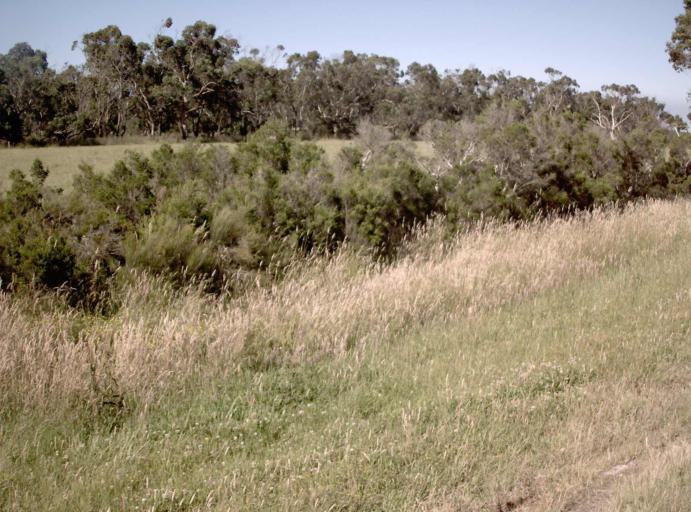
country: AU
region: Victoria
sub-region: Latrobe
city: Morwell
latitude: -38.6351
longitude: 146.5356
